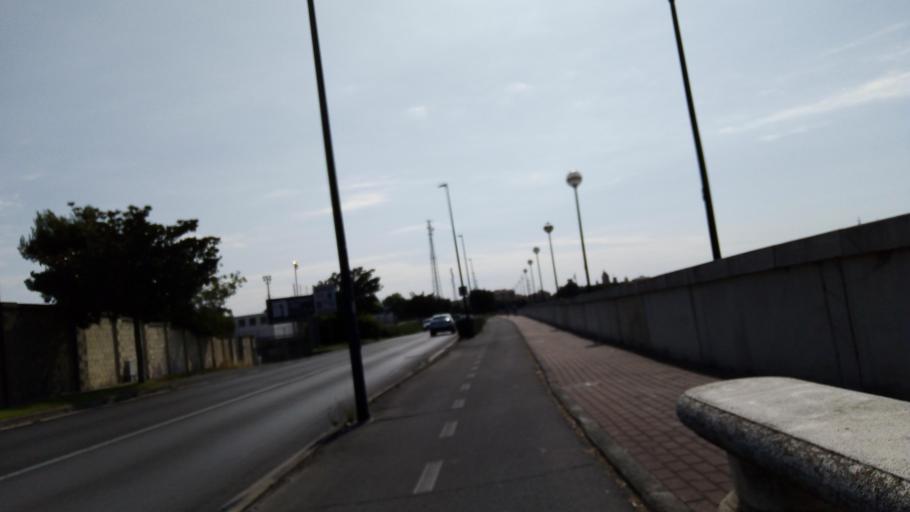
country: IT
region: Liguria
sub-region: Provincia di Savona
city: Albenga
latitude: 44.0532
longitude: 8.2020
